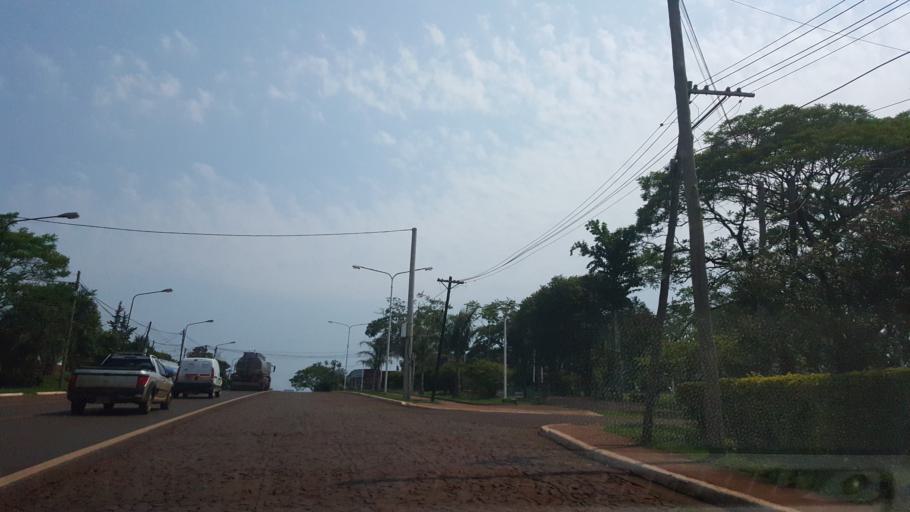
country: AR
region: Misiones
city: Gobernador Roca
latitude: -27.1898
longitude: -55.4684
